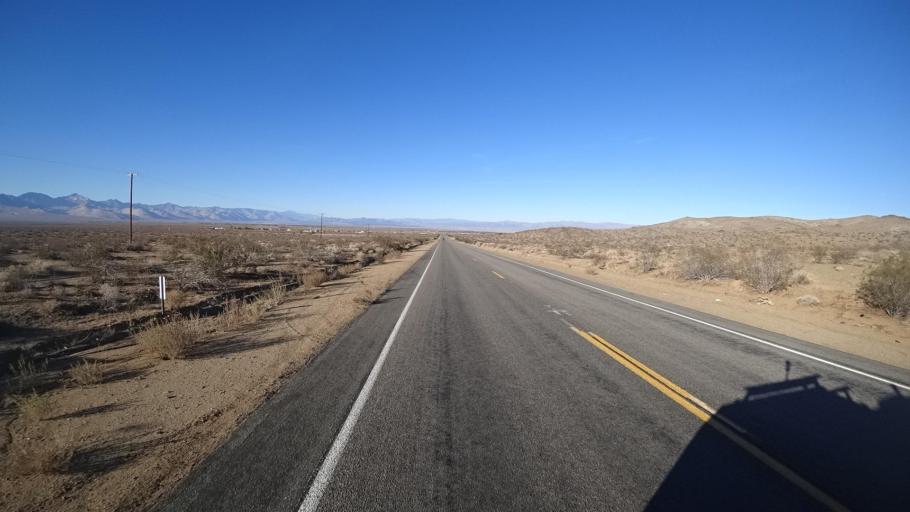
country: US
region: California
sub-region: Kern County
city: Ridgecrest
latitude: 35.5595
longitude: -117.7134
